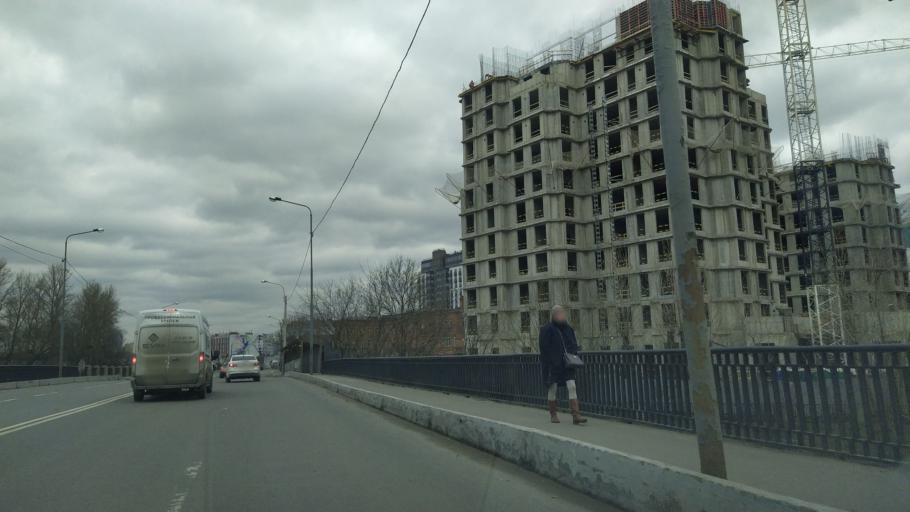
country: RU
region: St.-Petersburg
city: Centralniy
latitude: 59.9338
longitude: 30.4156
